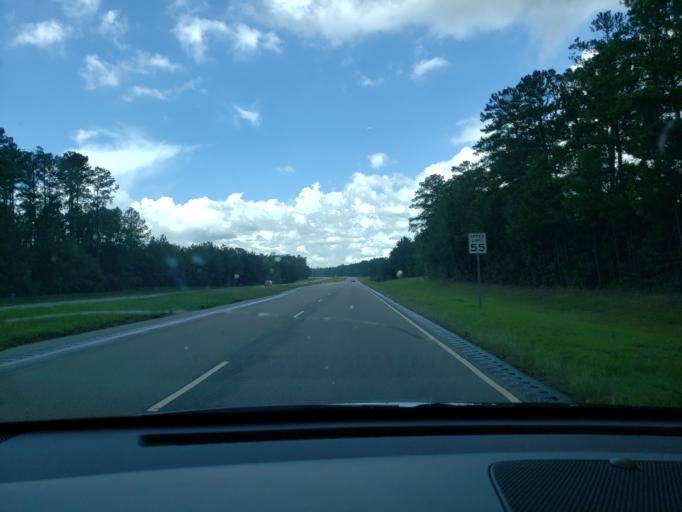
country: US
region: North Carolina
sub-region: Bladen County
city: Elizabethtown
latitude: 34.6267
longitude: -78.6518
